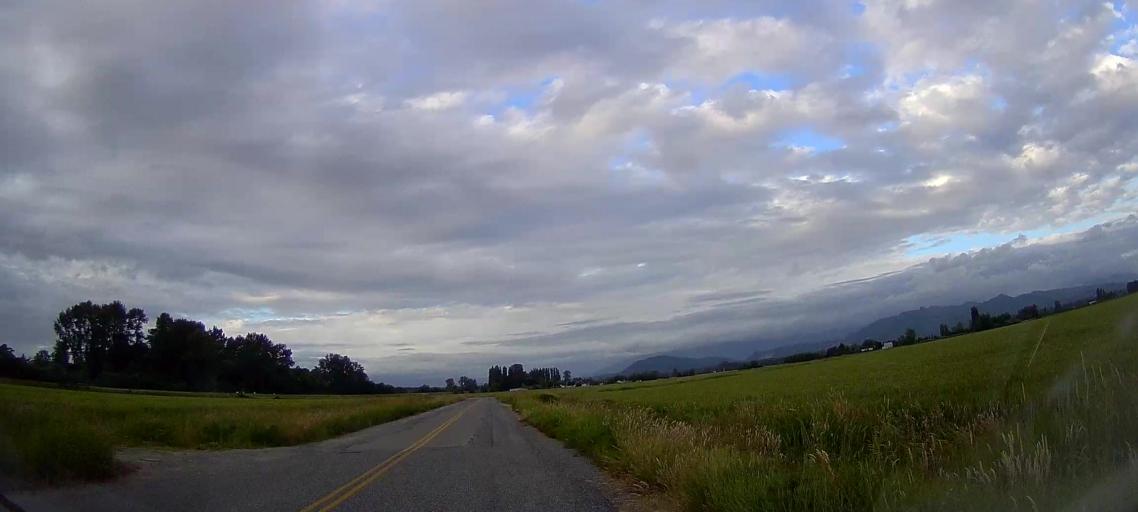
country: US
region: Washington
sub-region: Skagit County
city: Mount Vernon
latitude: 48.3604
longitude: -122.4174
